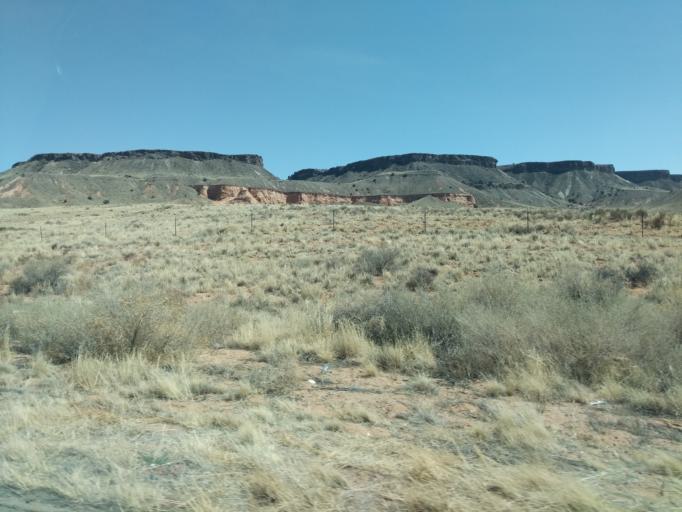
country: US
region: Arizona
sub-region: Navajo County
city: Dilkon
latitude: 35.4320
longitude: -110.0658
